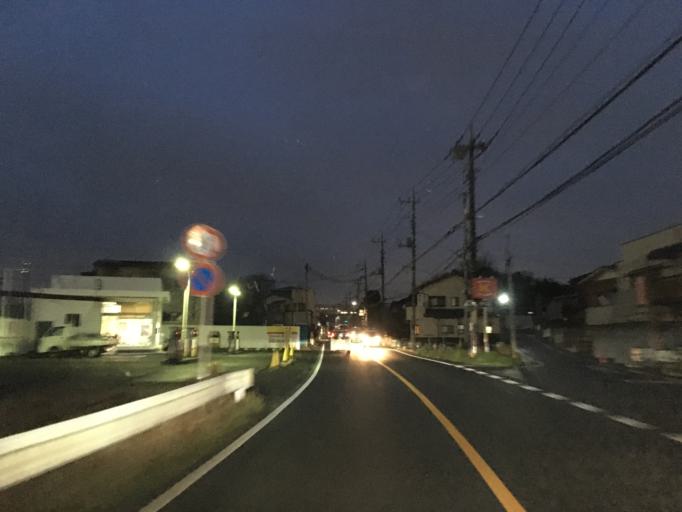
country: JP
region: Saitama
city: Oi
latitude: 35.8080
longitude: 139.5400
